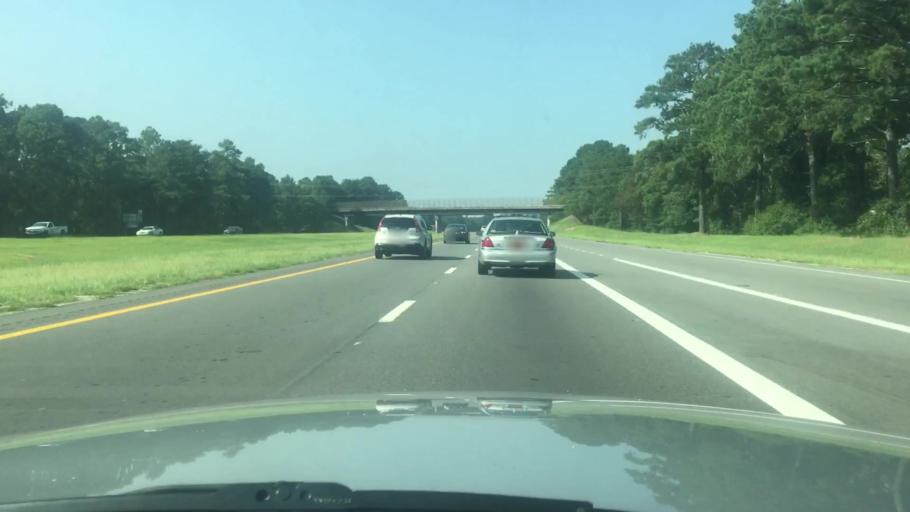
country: US
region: North Carolina
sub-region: Cumberland County
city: Vander
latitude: 34.9916
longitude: -78.8362
